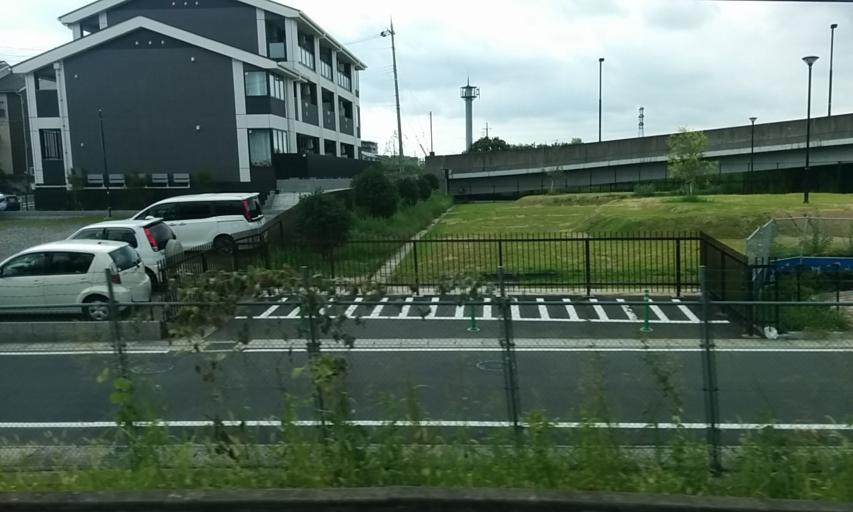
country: JP
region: Kyoto
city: Uji
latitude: 34.9318
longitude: 135.7889
